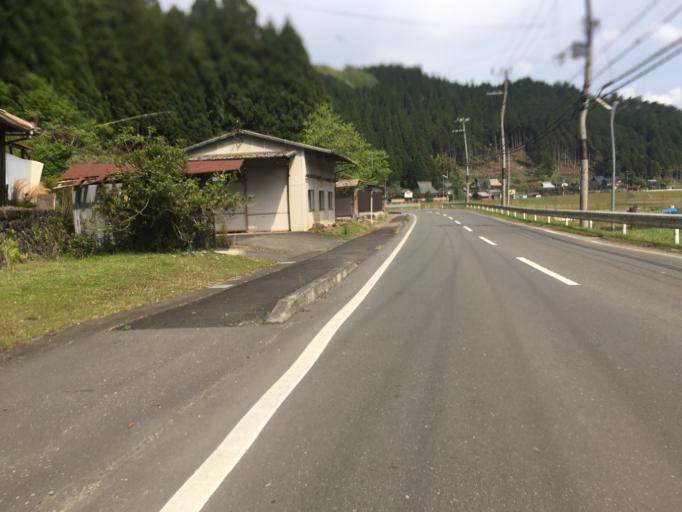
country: JP
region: Kyoto
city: Kameoka
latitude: 35.1440
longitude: 135.5872
